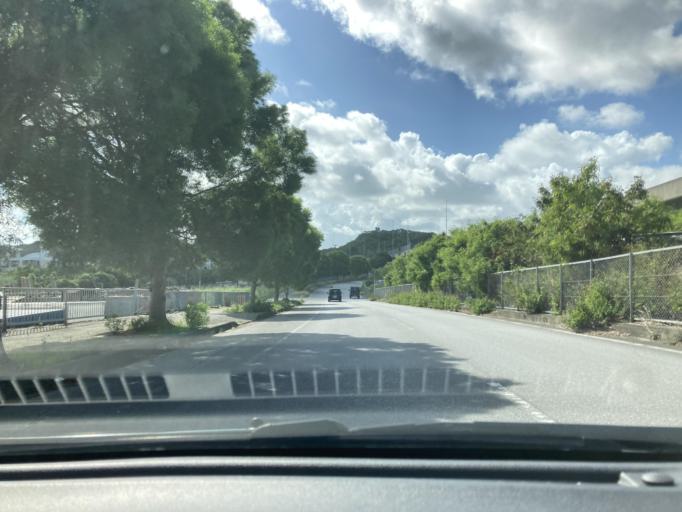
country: JP
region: Okinawa
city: Tomigusuku
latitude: 26.1810
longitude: 127.7221
